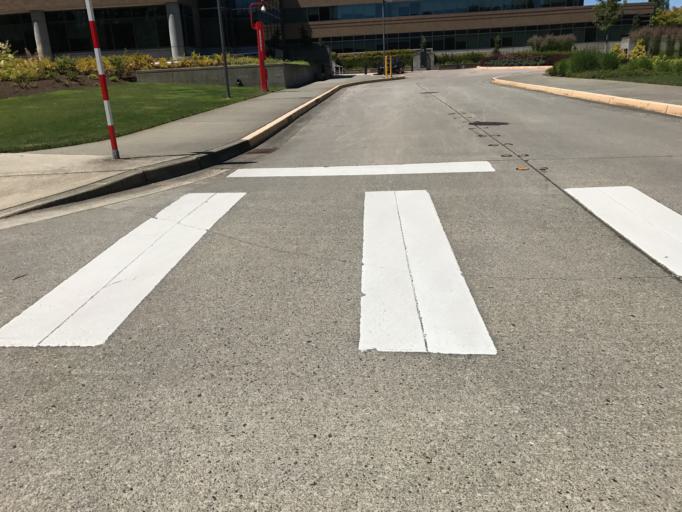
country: US
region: Washington
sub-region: King County
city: Redmond
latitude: 47.6443
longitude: -122.1271
